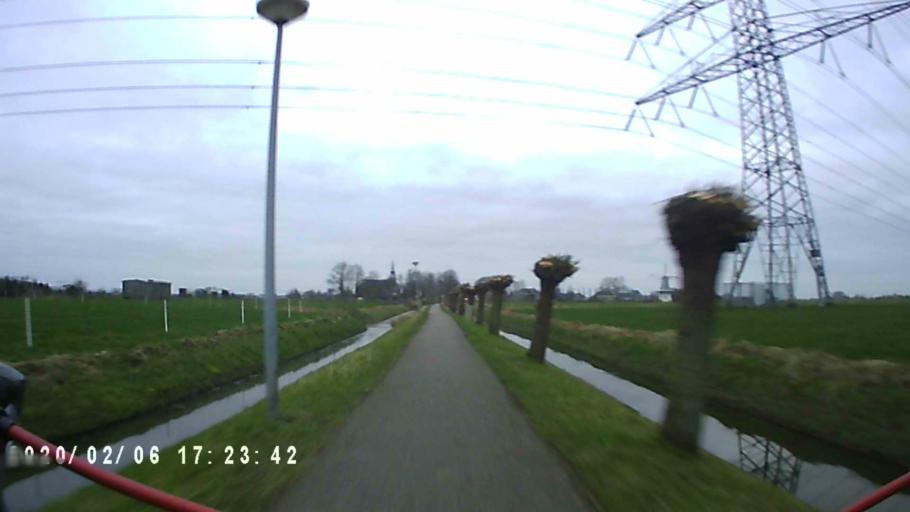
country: NL
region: Groningen
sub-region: Gemeente Winsum
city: Winsum
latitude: 53.2974
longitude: 6.5301
